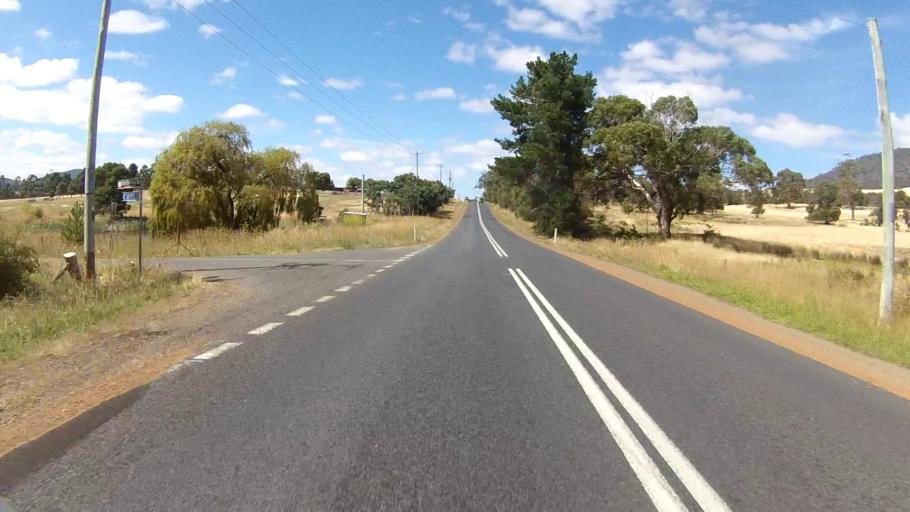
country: AU
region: Tasmania
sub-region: Sorell
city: Sorell
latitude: -42.6151
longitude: 147.4284
